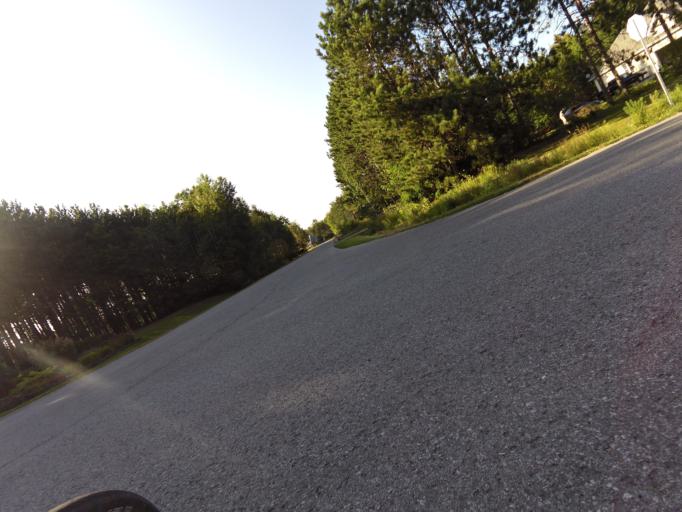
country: CA
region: Ontario
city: Bells Corners
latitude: 45.4695
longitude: -76.0334
